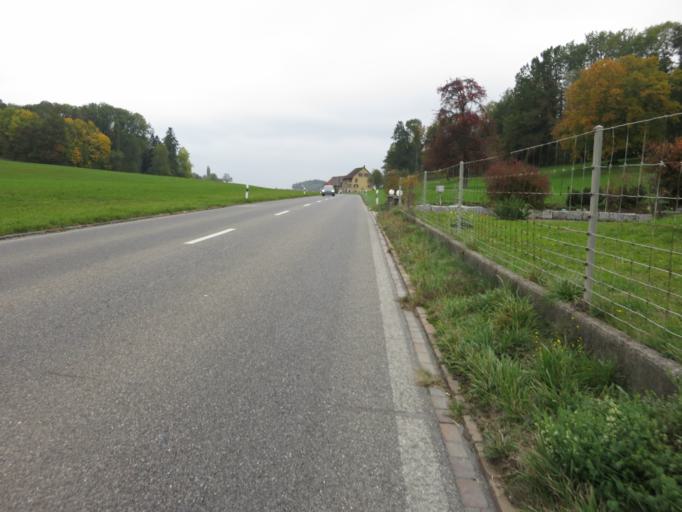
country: CH
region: Zurich
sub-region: Bezirk Hinwil
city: Bubikon
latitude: 47.2797
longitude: 8.8118
